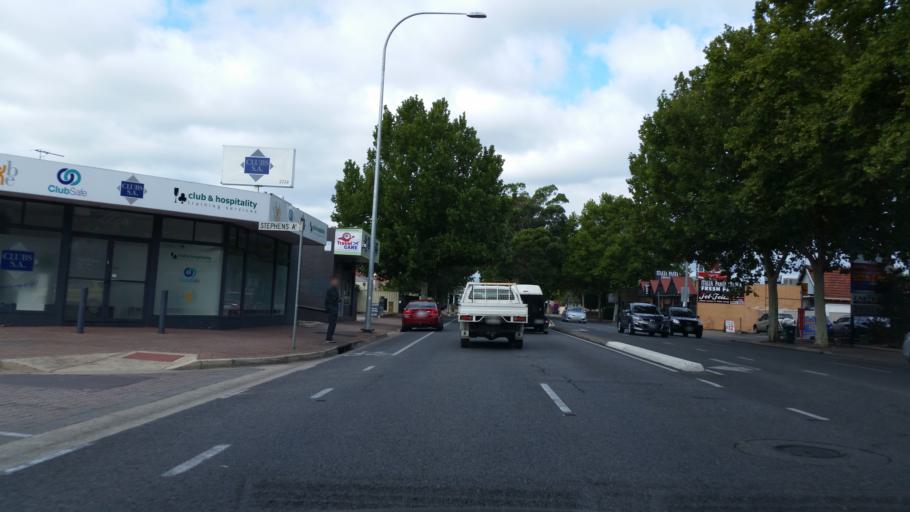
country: AU
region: South Australia
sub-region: City of West Torrens
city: Thebarton
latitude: -34.9244
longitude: 138.5557
